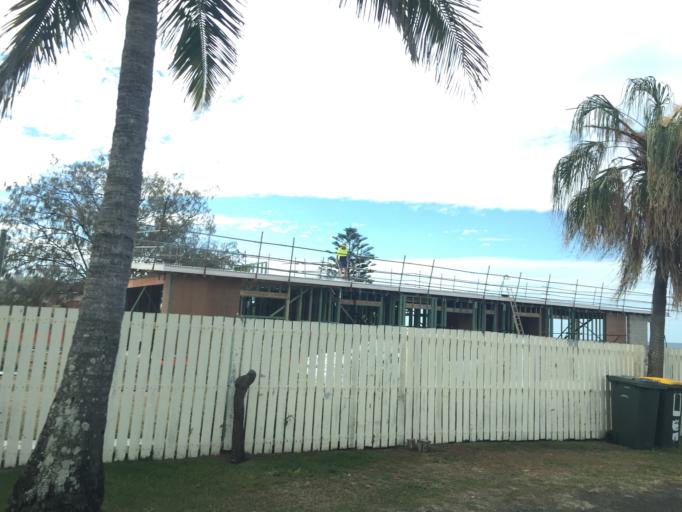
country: AU
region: Queensland
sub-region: Bundaberg
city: Bundaberg
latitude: -24.8337
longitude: 152.4716
